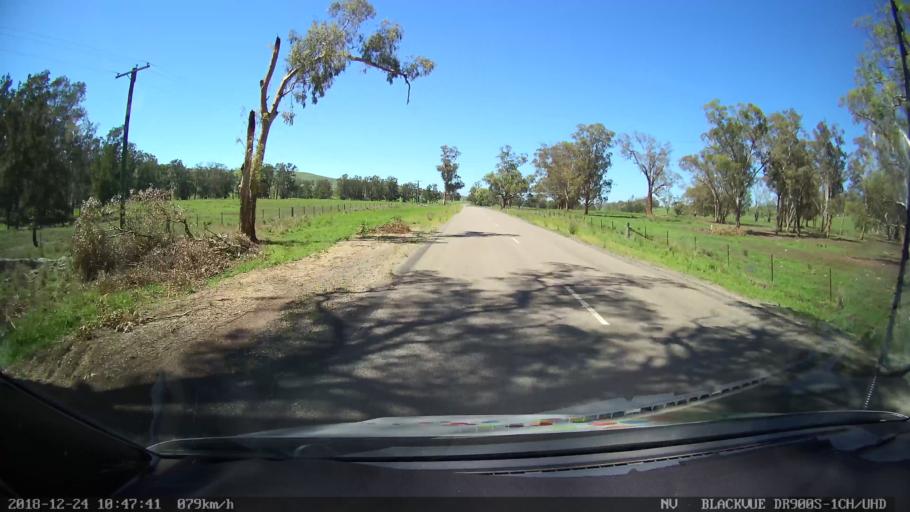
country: AU
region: New South Wales
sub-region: Upper Hunter Shire
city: Merriwa
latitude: -31.9272
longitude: 150.4297
